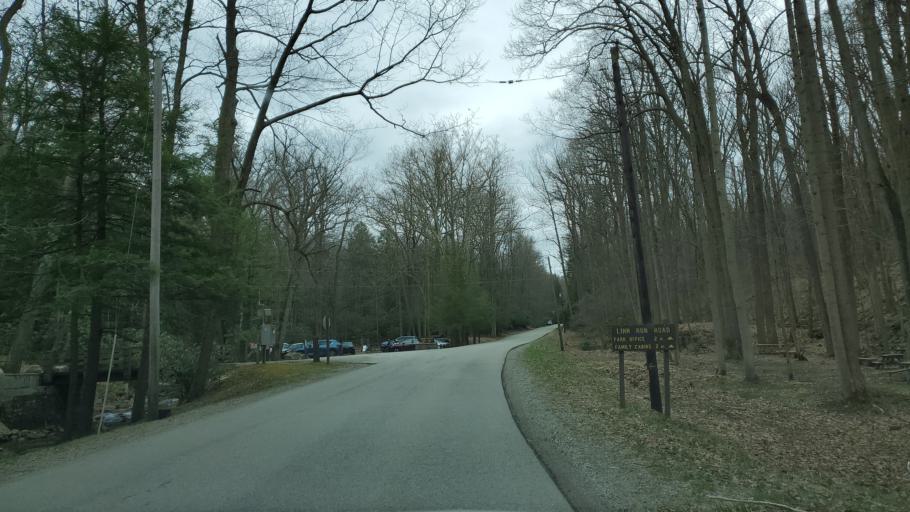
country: US
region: Pennsylvania
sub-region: Westmoreland County
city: Ligonier
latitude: 40.1694
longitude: -79.2341
